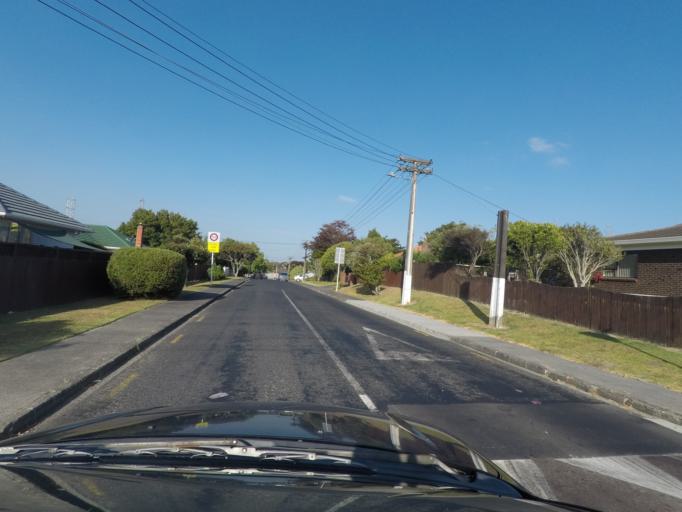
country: NZ
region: Auckland
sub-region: Auckland
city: Rosebank
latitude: -36.8621
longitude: 174.6455
